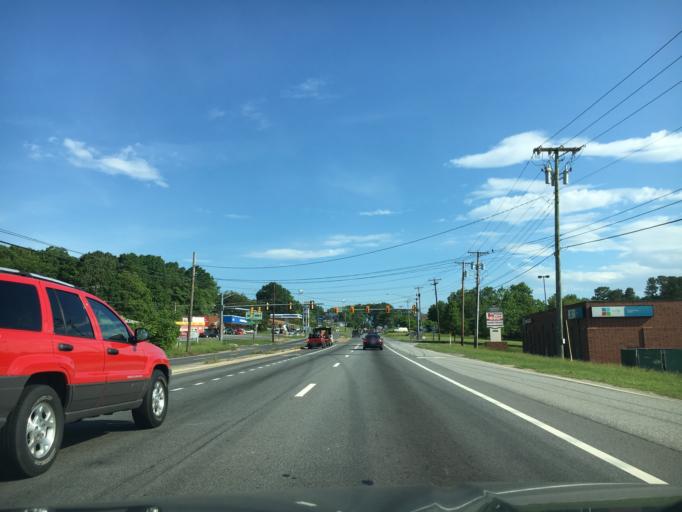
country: US
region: Virginia
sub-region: Campbell County
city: Timberlake
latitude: 37.3178
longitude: -79.1884
